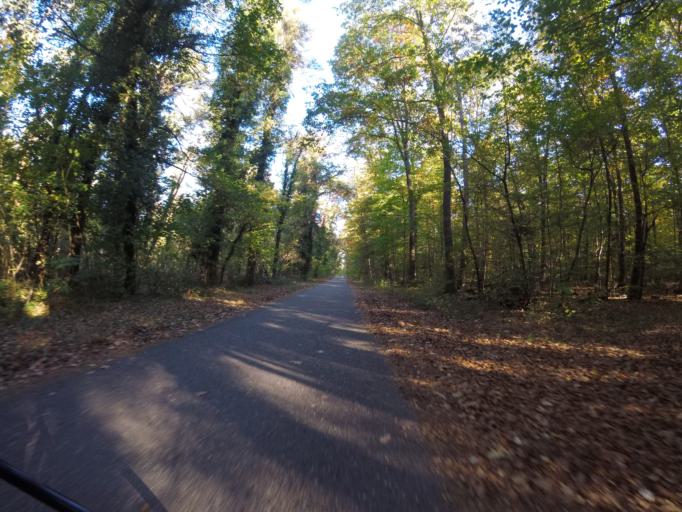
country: DE
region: Baden-Wuerttemberg
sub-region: Karlsruhe Region
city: Karlsruhe
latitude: 49.0467
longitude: 8.4079
